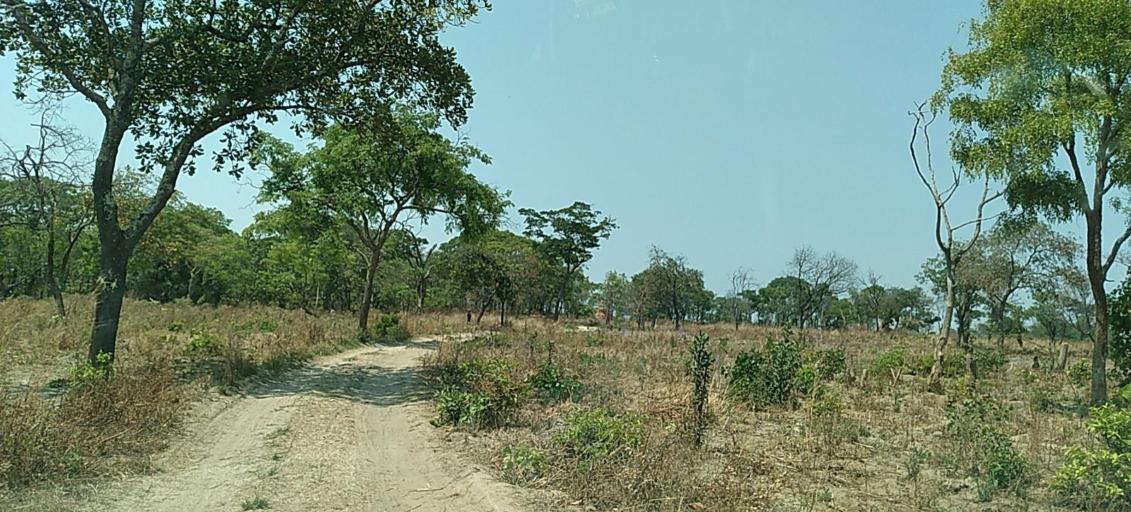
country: ZM
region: Copperbelt
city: Mpongwe
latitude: -13.8566
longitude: 28.0563
